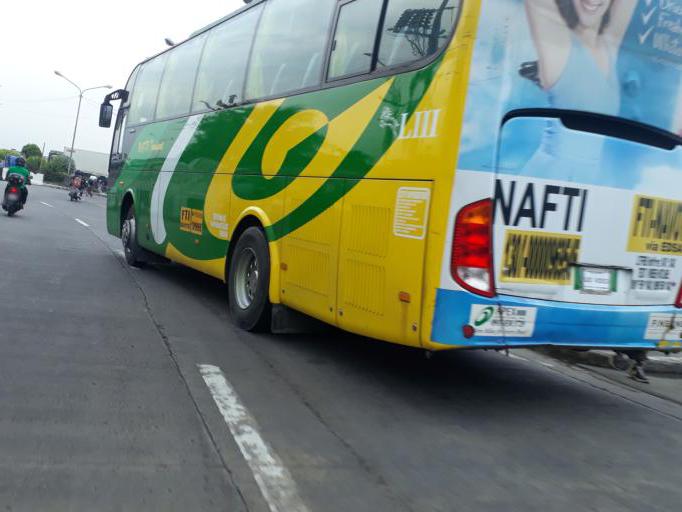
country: PH
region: Metro Manila
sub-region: Caloocan City
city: Niugan
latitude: 14.6519
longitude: 120.9481
